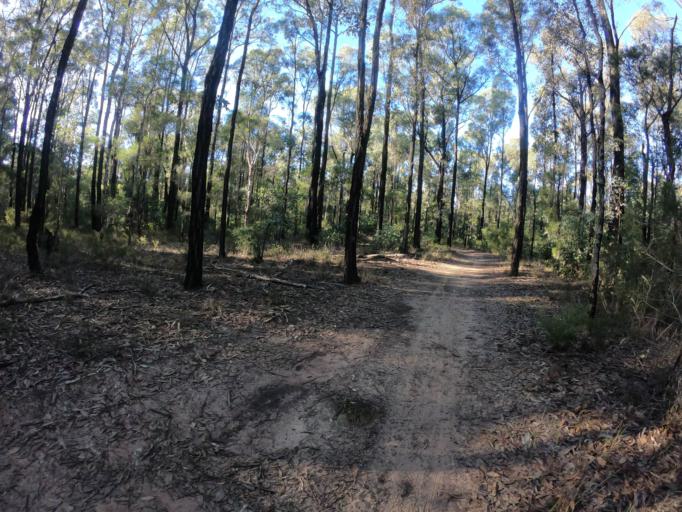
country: AU
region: New South Wales
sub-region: Hawkesbury
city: South Windsor
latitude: -33.6441
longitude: 150.7965
